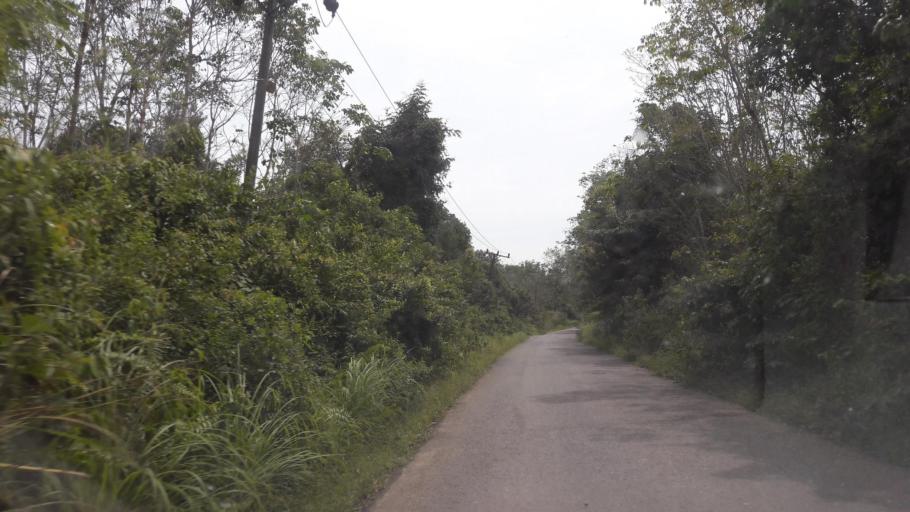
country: ID
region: South Sumatra
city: Gunungmenang
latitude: -3.1321
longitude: 104.1112
